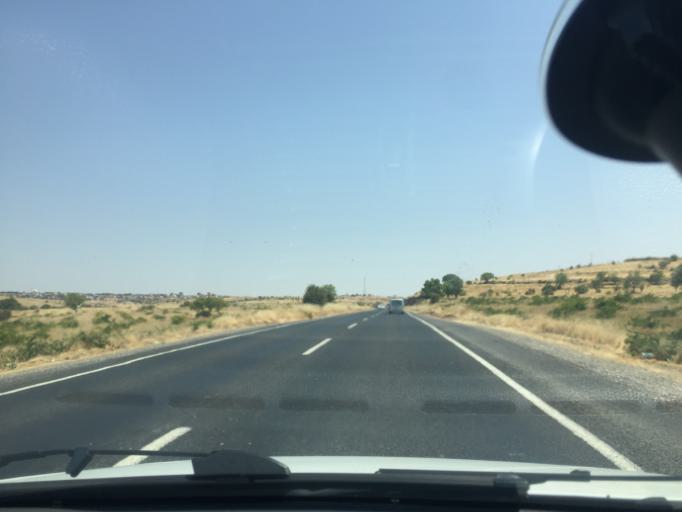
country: TR
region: Mardin
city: Acirli
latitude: 37.4503
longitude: 41.2658
